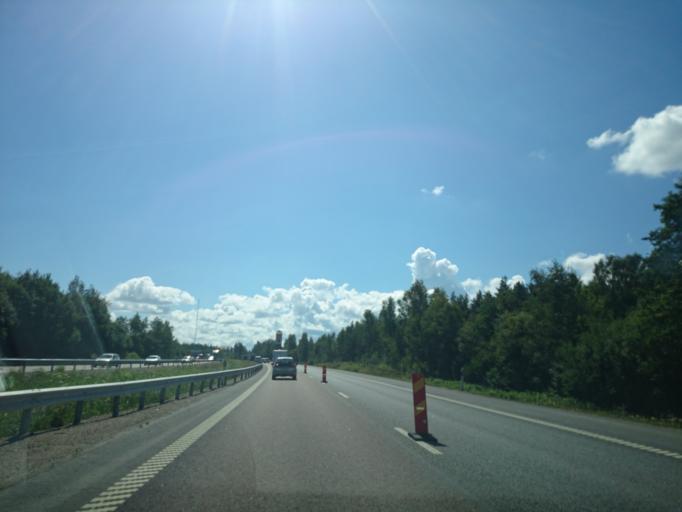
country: SE
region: Gaevleborg
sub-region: Gavle Kommun
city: Gavle
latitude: 60.6554
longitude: 17.1145
